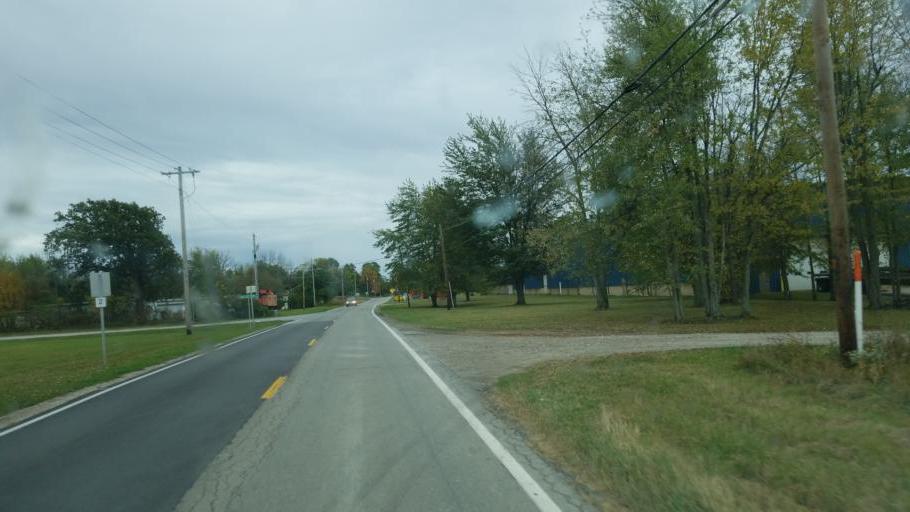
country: US
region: Ohio
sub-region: Huron County
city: New London
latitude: 41.0944
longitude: -82.4018
